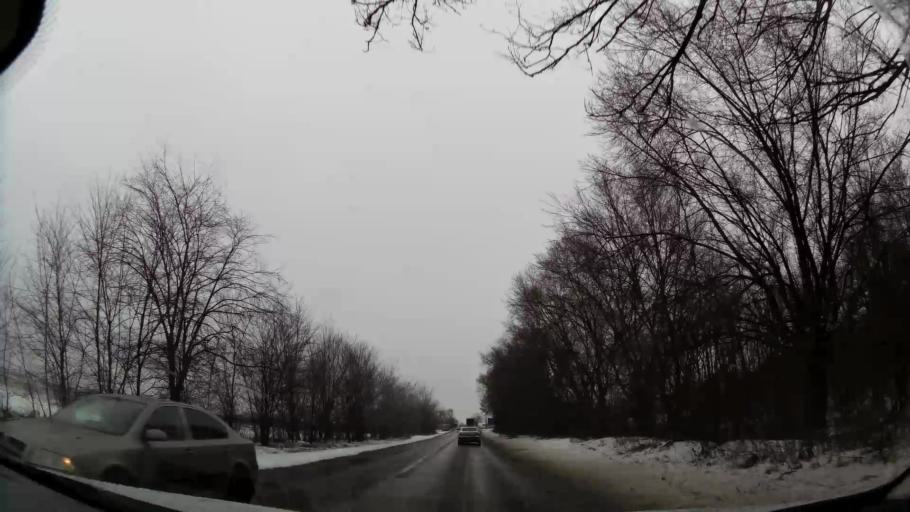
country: RO
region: Dambovita
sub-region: Comuna Ulmi
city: Ulmi
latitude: 44.8965
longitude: 25.5082
